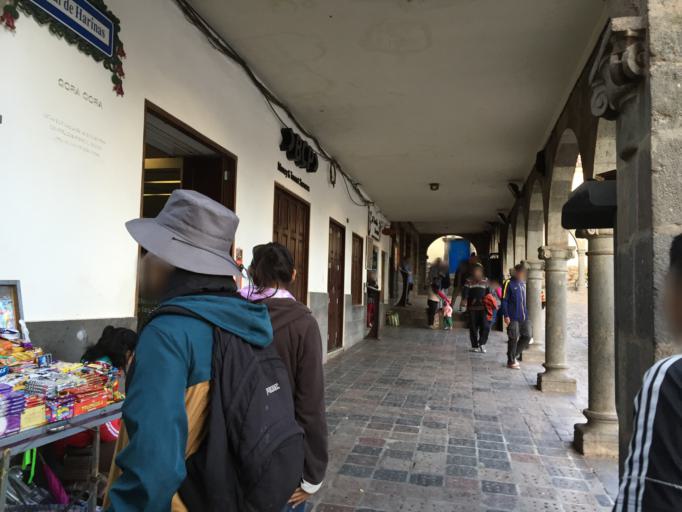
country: PE
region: Cusco
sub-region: Provincia de Cusco
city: Cusco
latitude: -13.5160
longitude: -71.9791
